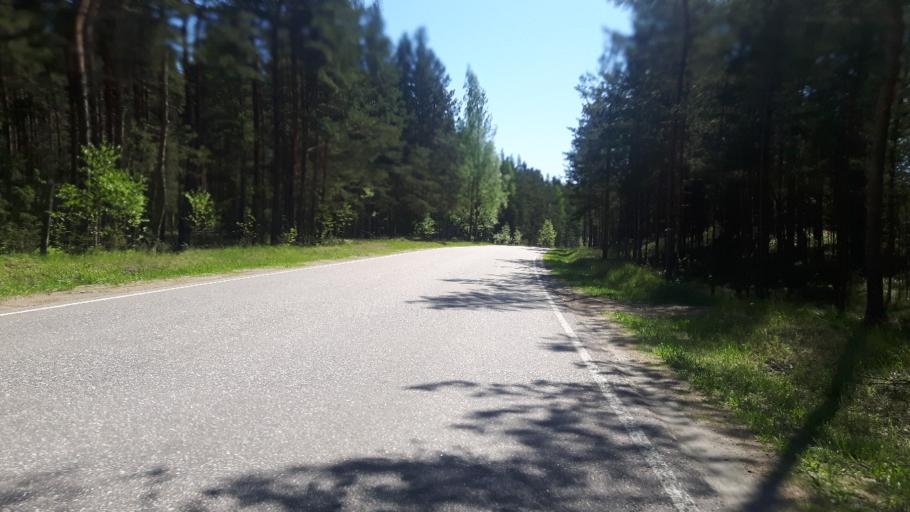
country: RU
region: Leningrad
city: Glebychevo
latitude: 60.3306
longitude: 28.8225
